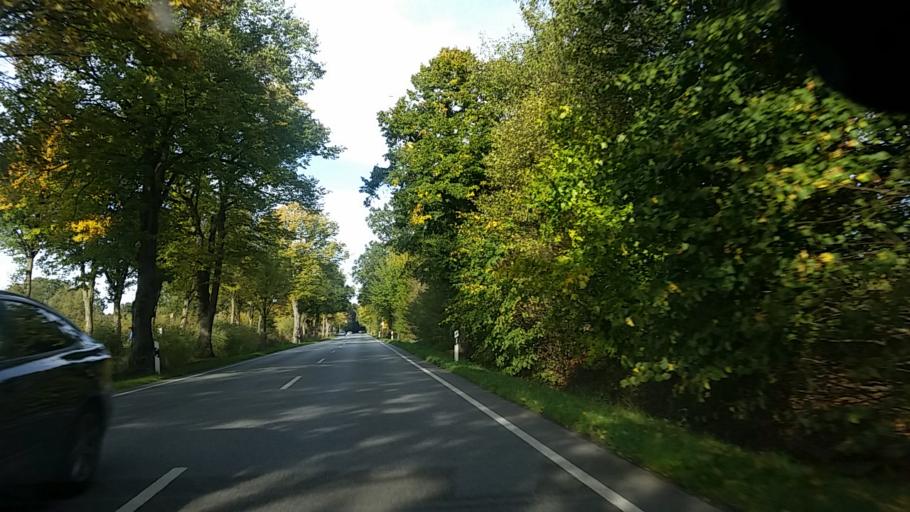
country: DE
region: Schleswig-Holstein
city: Delingsdorf
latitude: 53.7173
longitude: 10.2505
